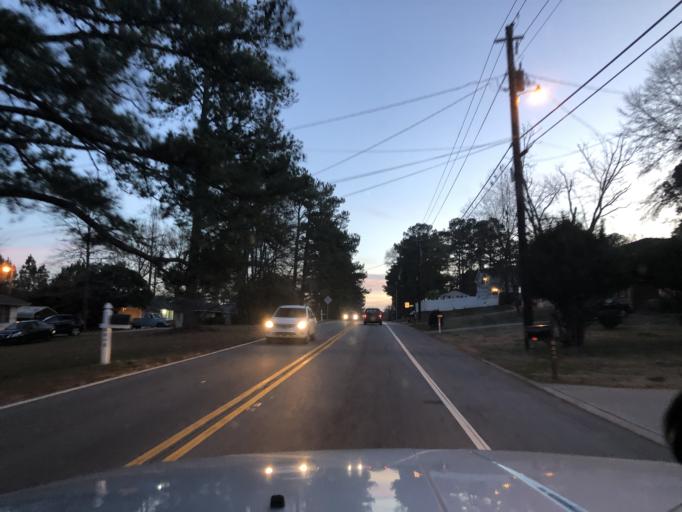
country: US
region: Georgia
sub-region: Clayton County
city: Jonesboro
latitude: 33.5242
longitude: -84.3909
